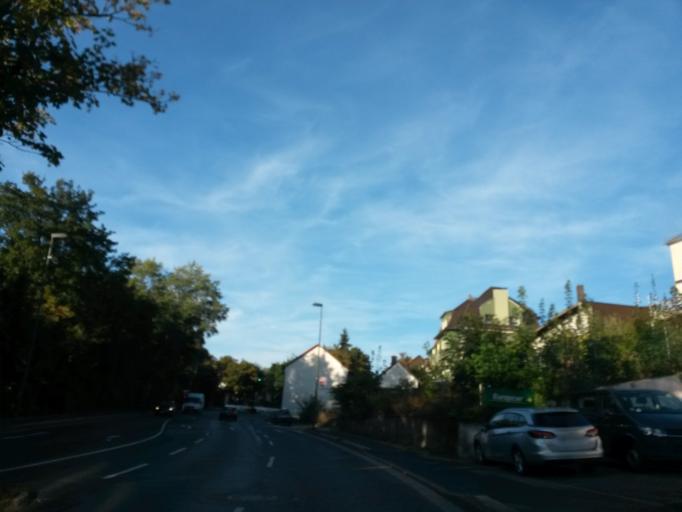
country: DE
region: North Rhine-Westphalia
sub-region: Regierungsbezirk Arnsberg
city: Luedenscheid
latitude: 51.2272
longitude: 7.6461
